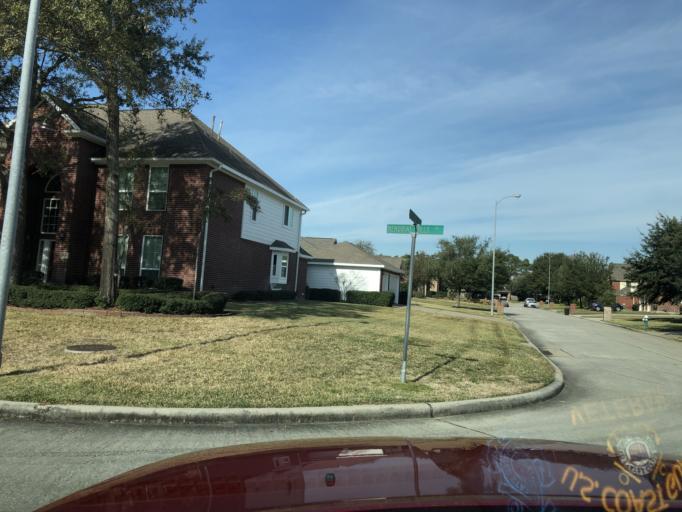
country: US
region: Texas
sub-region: Harris County
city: Tomball
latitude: 30.0272
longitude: -95.5561
